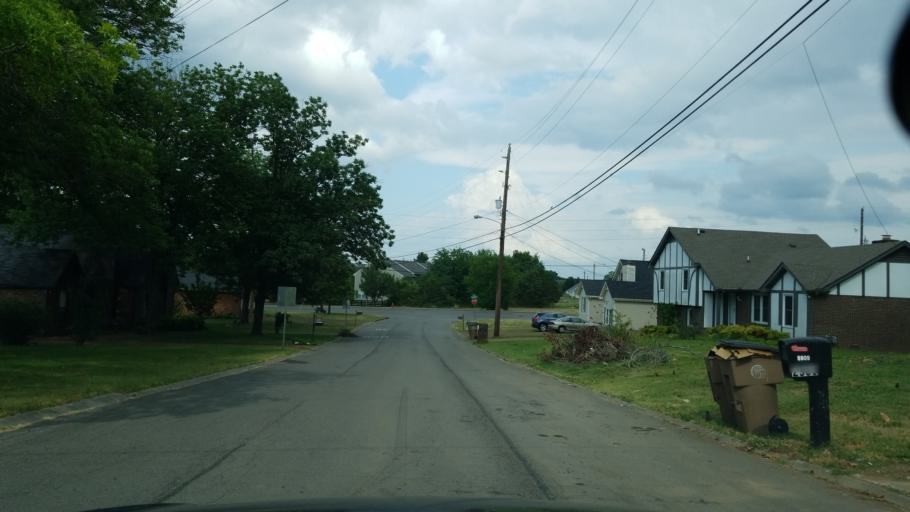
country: US
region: Tennessee
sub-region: Rutherford County
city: La Vergne
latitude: 36.0839
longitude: -86.6069
